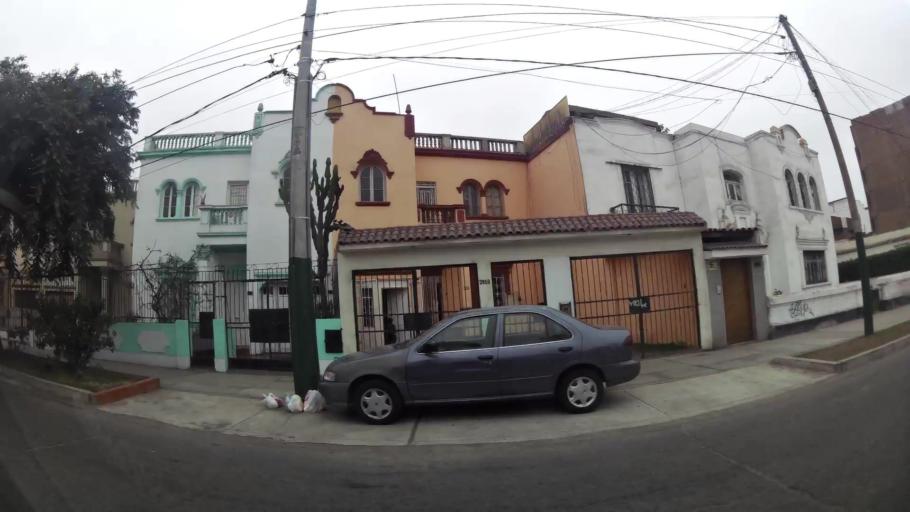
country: PE
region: Lima
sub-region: Lima
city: San Isidro
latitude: -12.0952
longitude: -77.0703
